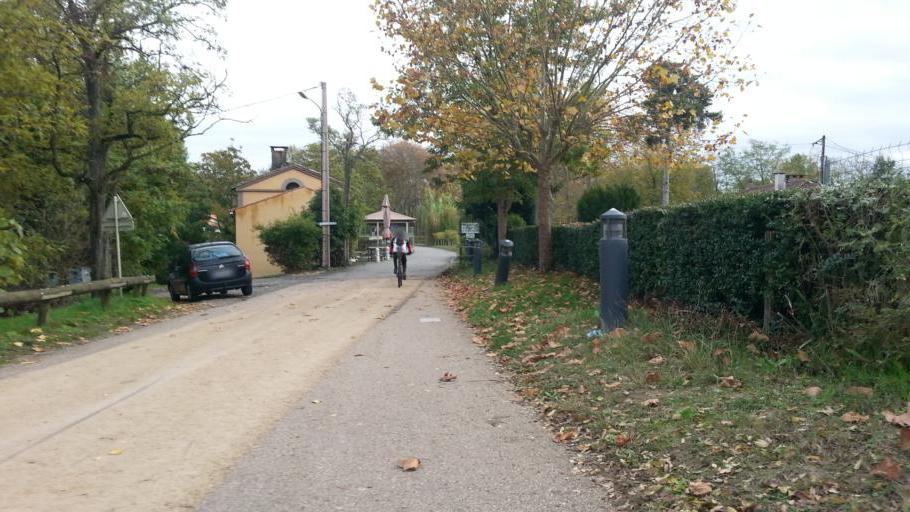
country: FR
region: Midi-Pyrenees
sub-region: Departement de la Haute-Garonne
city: Labege
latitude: 43.5240
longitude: 1.5188
